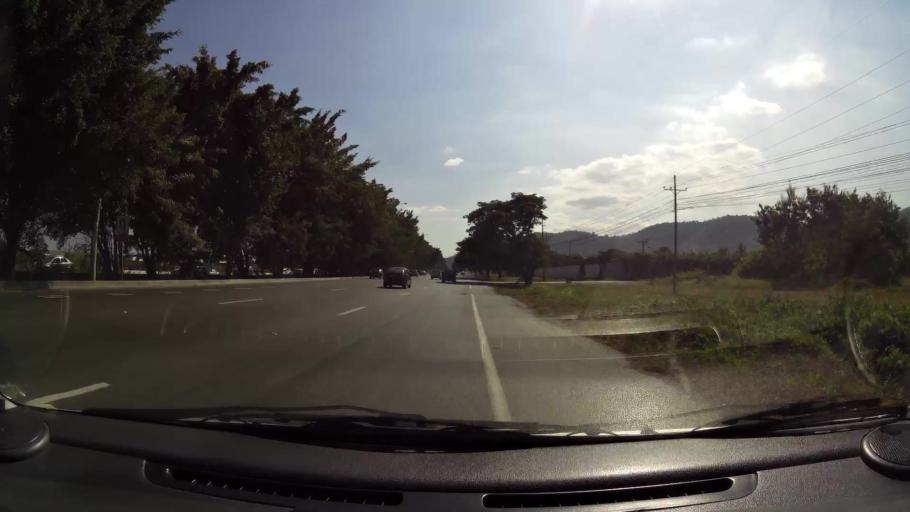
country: EC
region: Guayas
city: Santa Lucia
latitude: -2.1848
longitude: -79.9735
